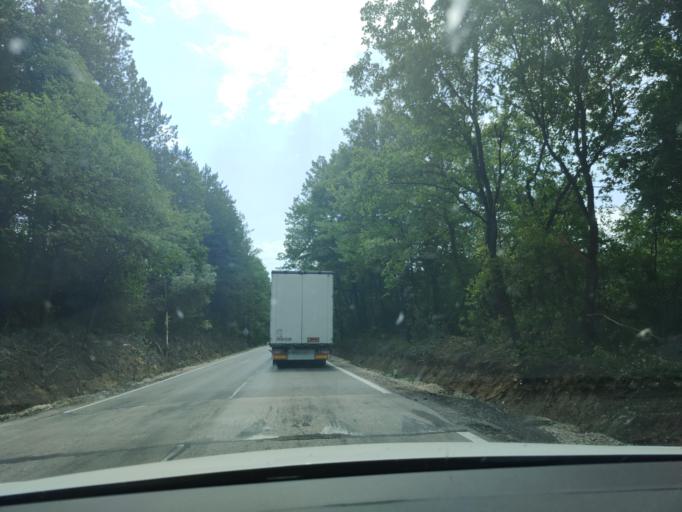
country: BG
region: Vidin
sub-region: Obshtina Dimovo
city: Dimovo
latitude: 43.6781
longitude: 22.7684
